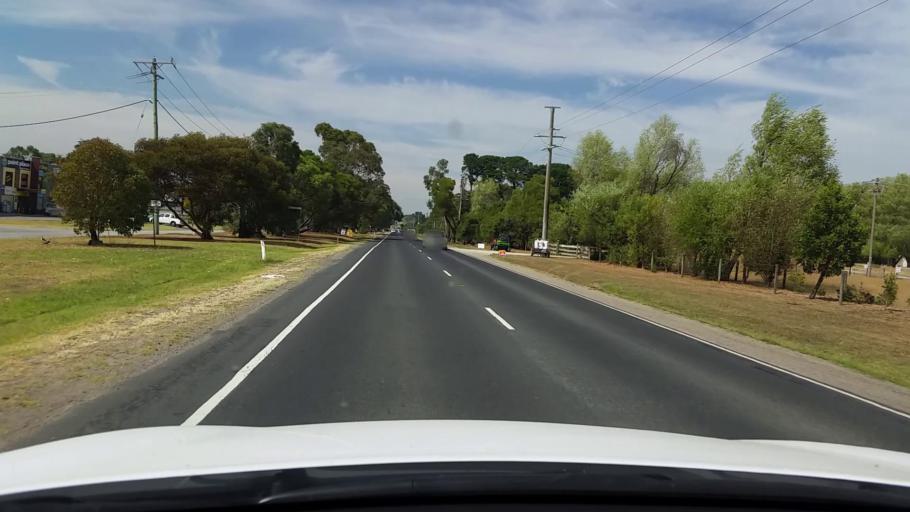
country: AU
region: Victoria
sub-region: Mornington Peninsula
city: Hastings
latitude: -38.2906
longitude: 145.1836
